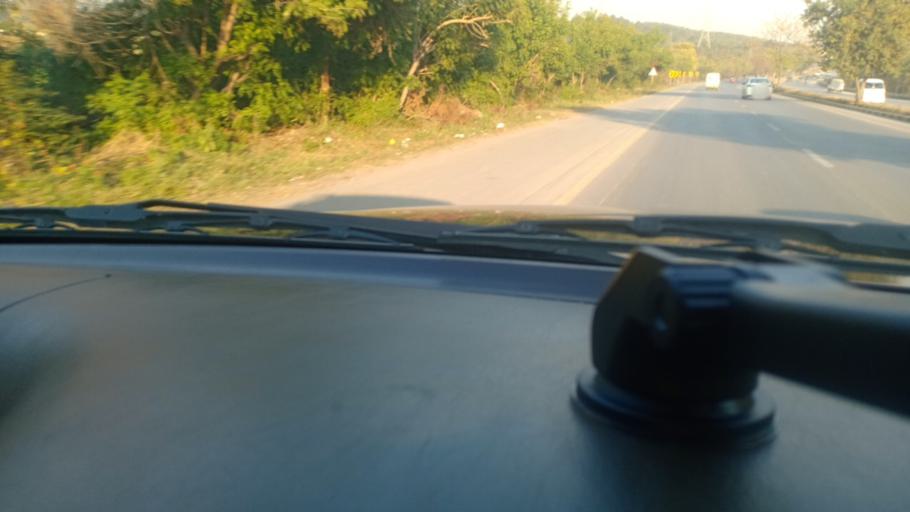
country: PK
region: Islamabad
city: Islamabad
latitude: 33.7340
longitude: 73.1541
